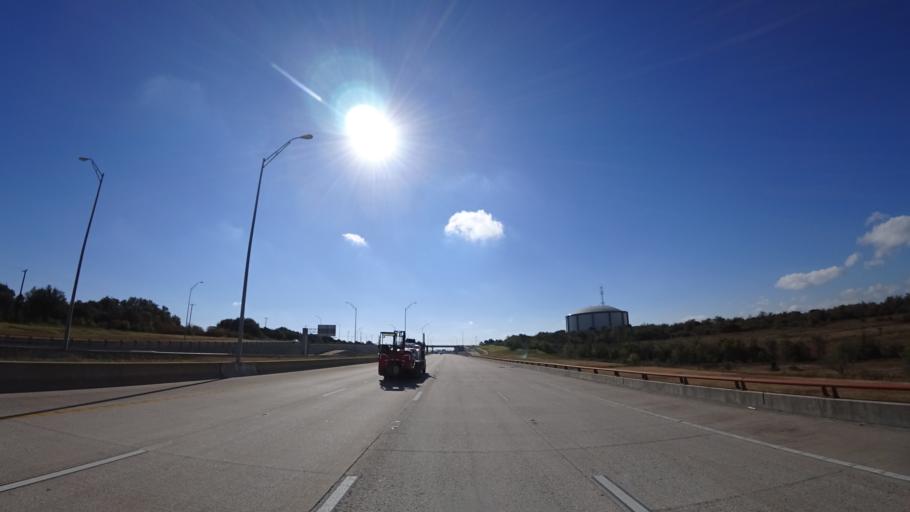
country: US
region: Texas
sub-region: Travis County
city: Wells Branch
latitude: 30.4645
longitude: -97.7009
